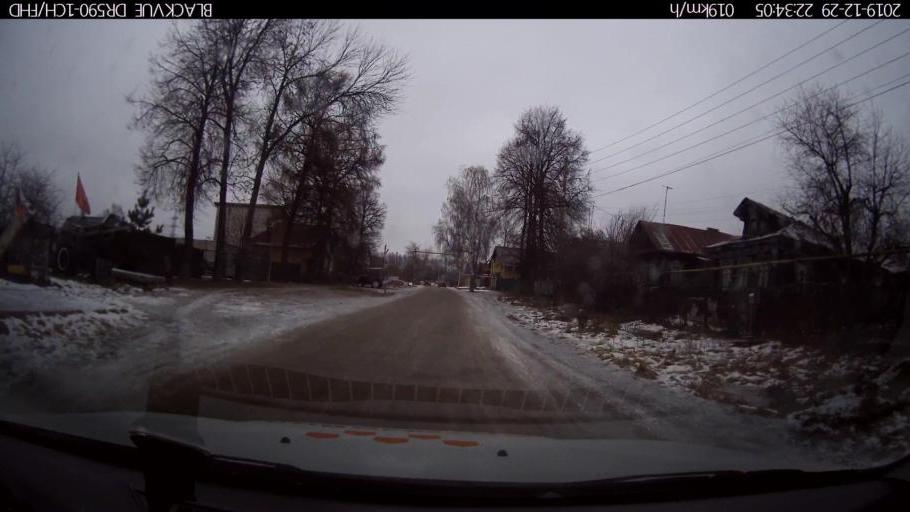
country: RU
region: Nizjnij Novgorod
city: Afonino
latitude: 56.2037
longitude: 43.9861
